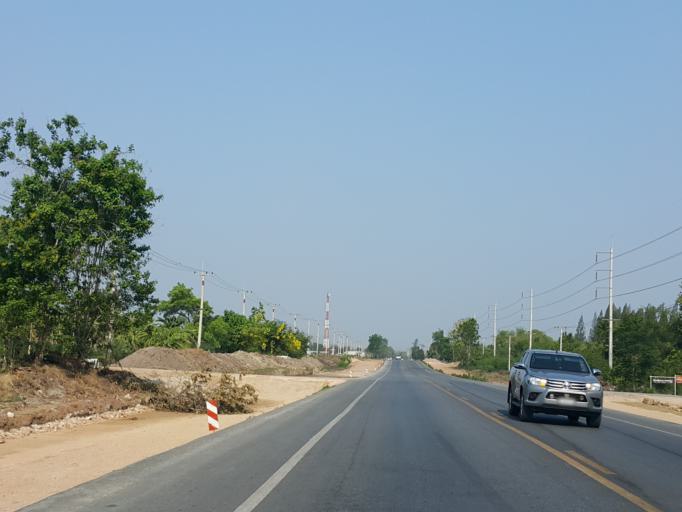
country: TH
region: Kanchanaburi
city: Sai Yok
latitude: 14.0880
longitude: 99.3313
